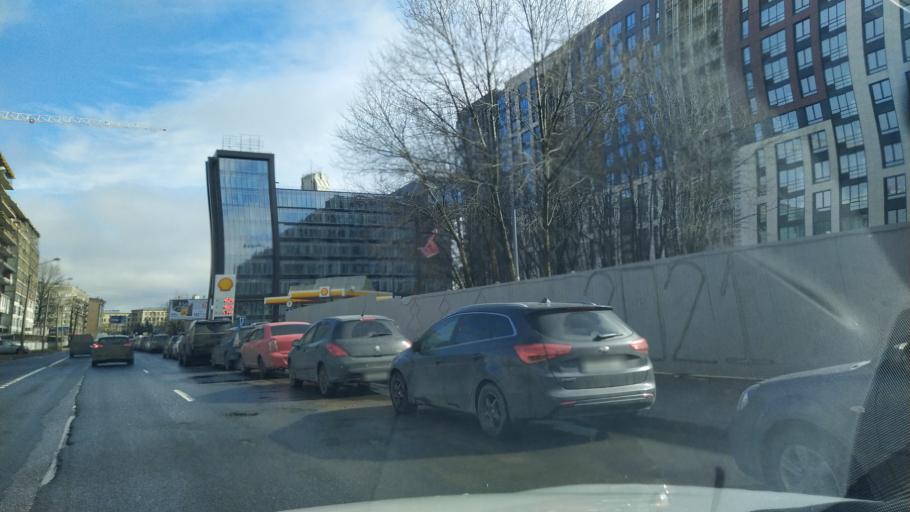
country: RU
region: Leningrad
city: Sampsonievskiy
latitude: 59.9858
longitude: 30.3255
